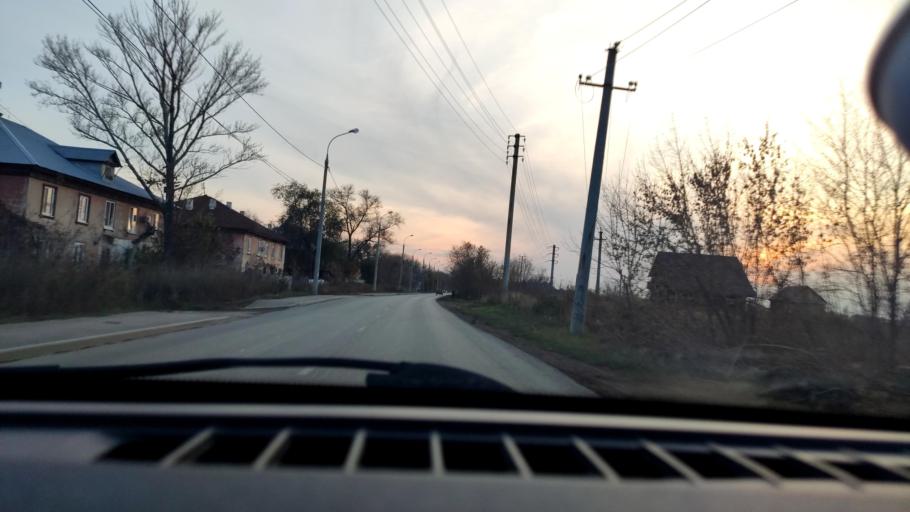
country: RU
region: Samara
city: Samara
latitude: 53.1409
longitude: 50.1306
